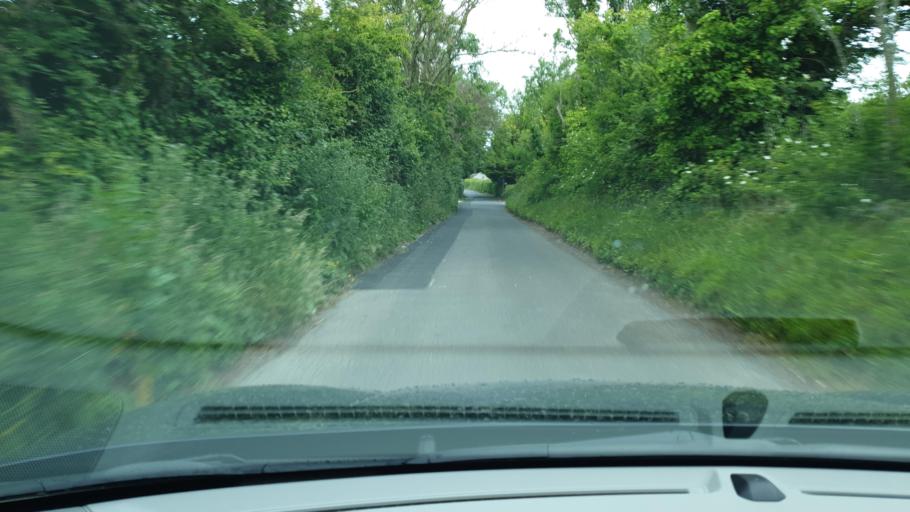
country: IE
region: Leinster
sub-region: An Mhi
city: Ashbourne
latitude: 53.5114
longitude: -6.3845
